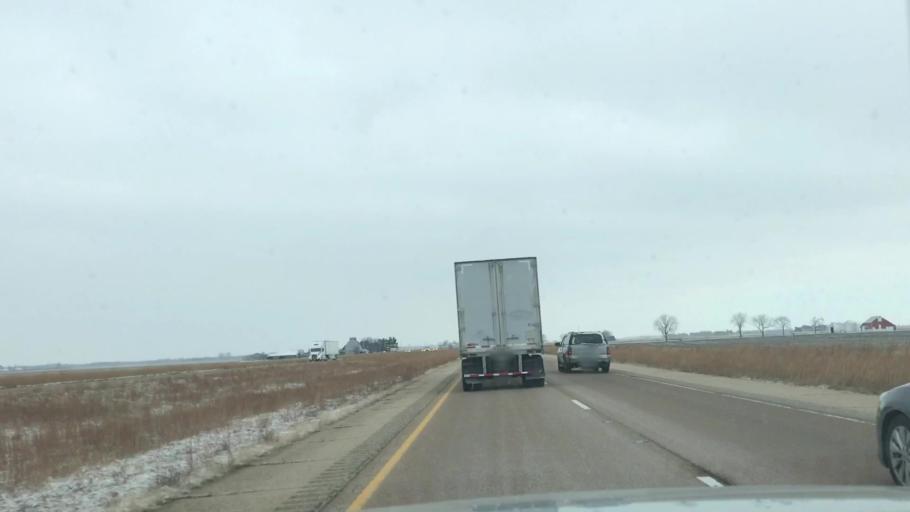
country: US
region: Illinois
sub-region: Montgomery County
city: Raymond
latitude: 39.3804
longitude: -89.6429
